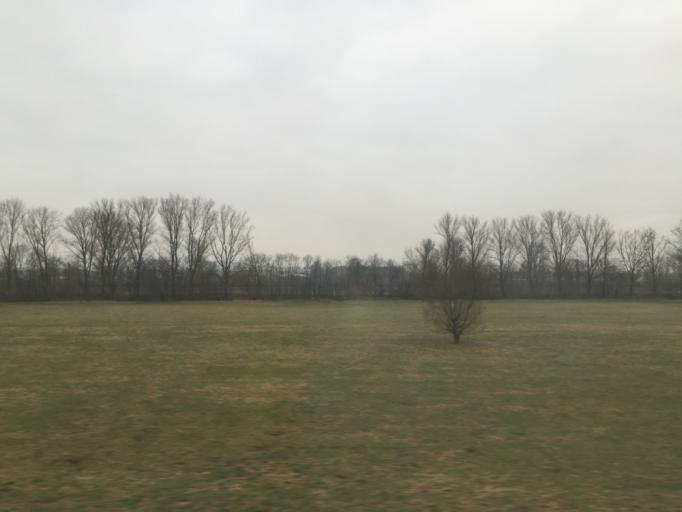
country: DE
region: Baden-Wuerttemberg
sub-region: Regierungsbezirk Stuttgart
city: Nordheim
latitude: 49.1154
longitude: 9.1543
